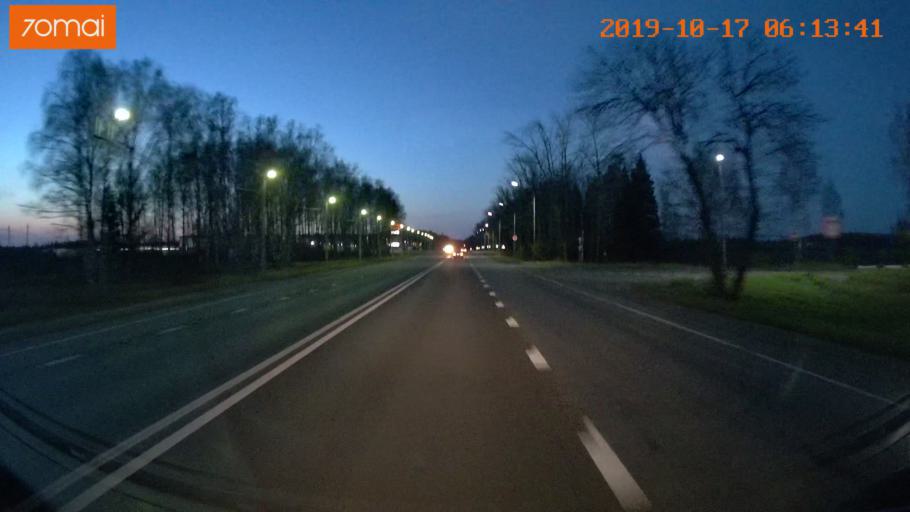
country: RU
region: Ivanovo
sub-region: Gorod Ivanovo
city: Ivanovo
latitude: 56.8953
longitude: 40.9372
